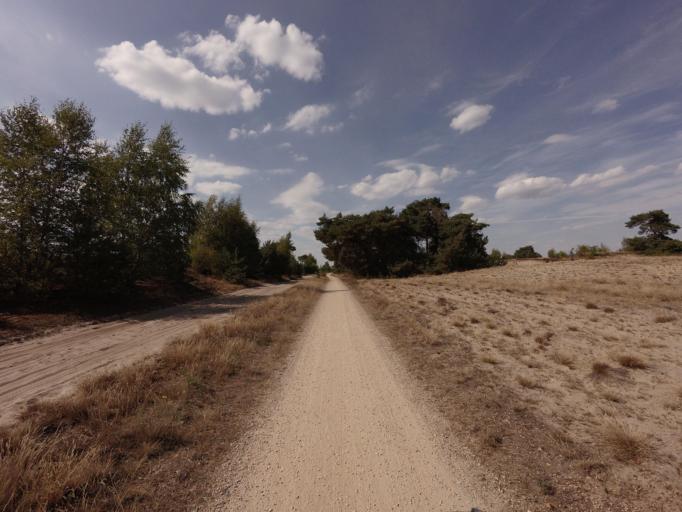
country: NL
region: North Brabant
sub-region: Gemeente Cranendonck
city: Cranendonck
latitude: 51.3031
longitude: 5.5280
